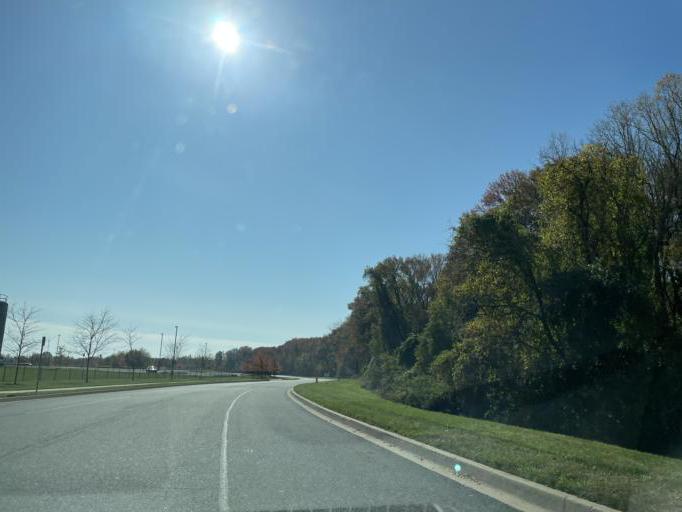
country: US
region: Maryland
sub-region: Harford County
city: Edgewood
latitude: 39.4155
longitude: -76.3133
